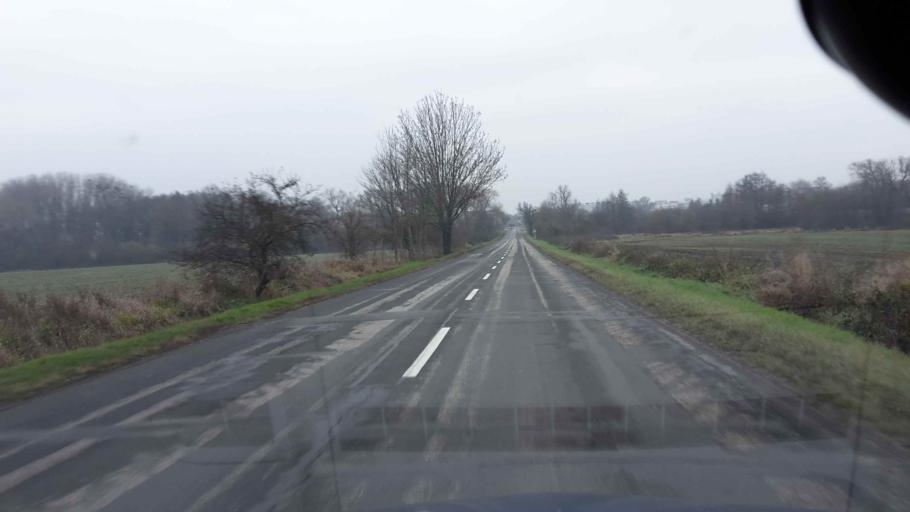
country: CZ
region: Olomoucky
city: Horka nad Moravou
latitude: 49.6091
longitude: 17.2086
